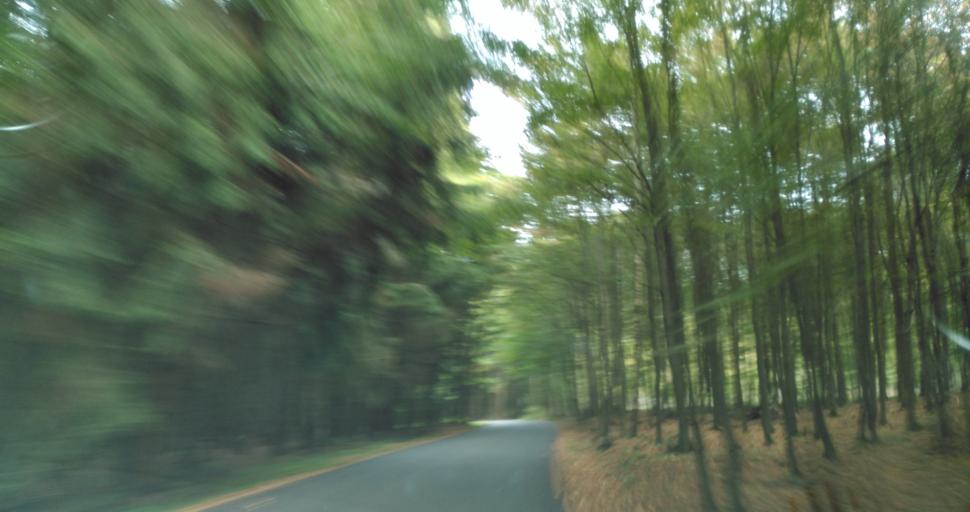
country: CZ
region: Plzensky
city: Zbiroh
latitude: 49.9301
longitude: 13.7883
